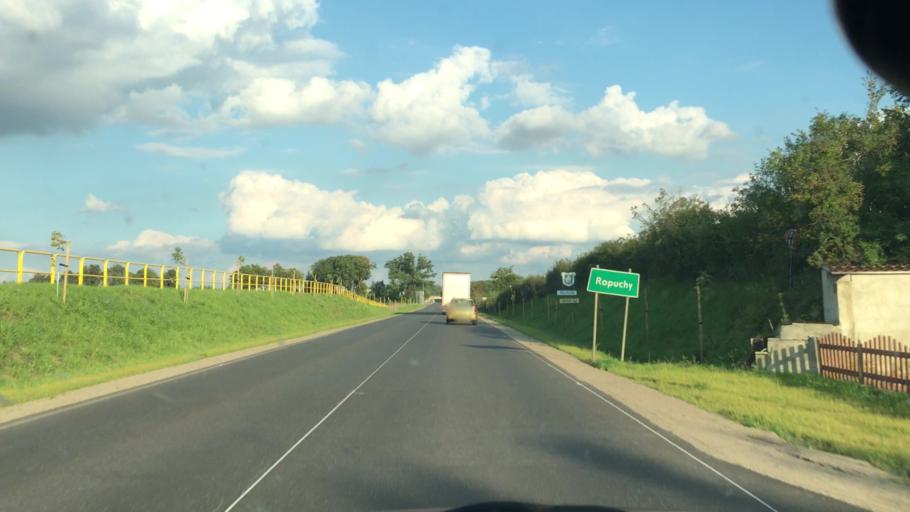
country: PL
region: Pomeranian Voivodeship
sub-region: Powiat tczewski
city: Pelplin
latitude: 53.9280
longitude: 18.6314
